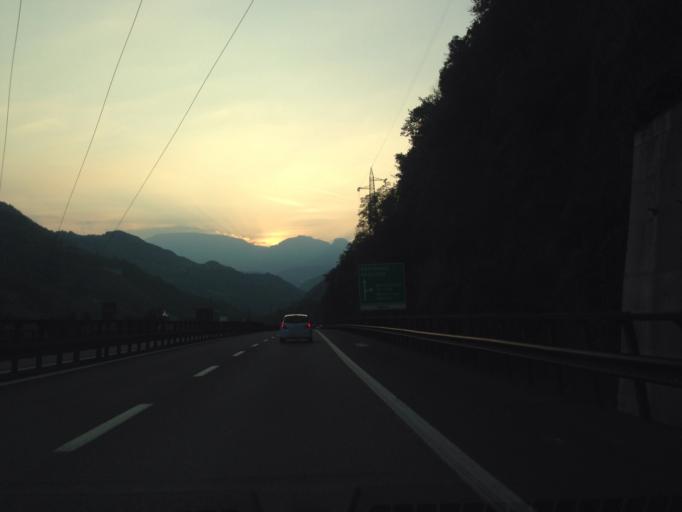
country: IT
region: Trentino-Alto Adige
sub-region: Bolzano
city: Cardano
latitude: 46.4932
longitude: 11.3784
